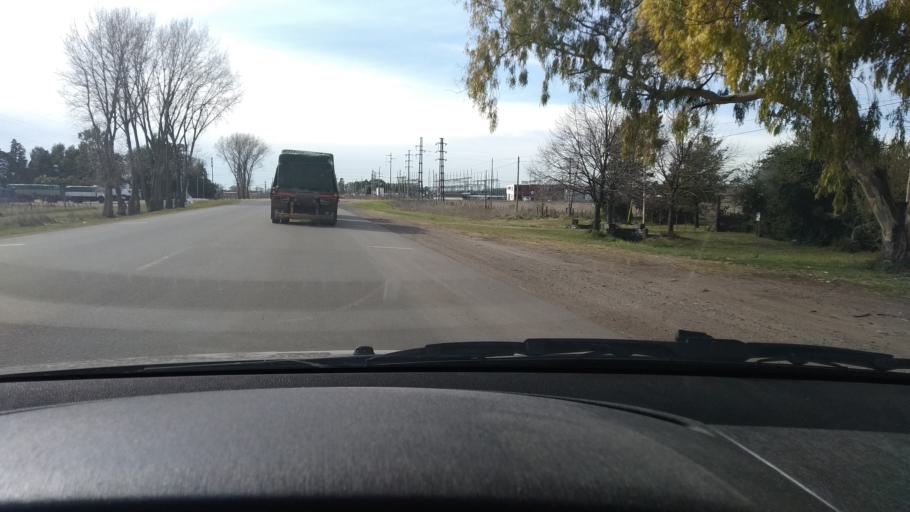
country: AR
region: Buenos Aires
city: Olavarria
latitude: -36.9467
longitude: -60.2427
